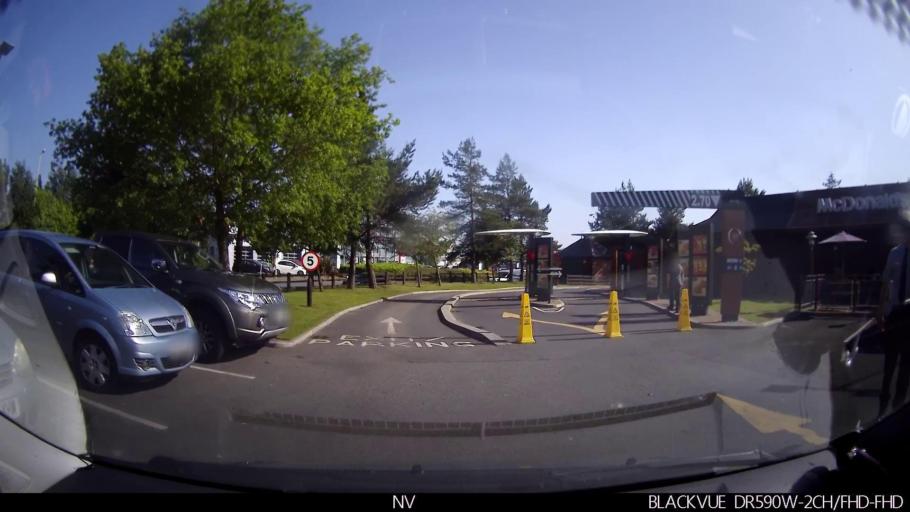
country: GB
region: England
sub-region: North Yorkshire
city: Scarborough
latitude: 54.2371
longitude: -0.4180
